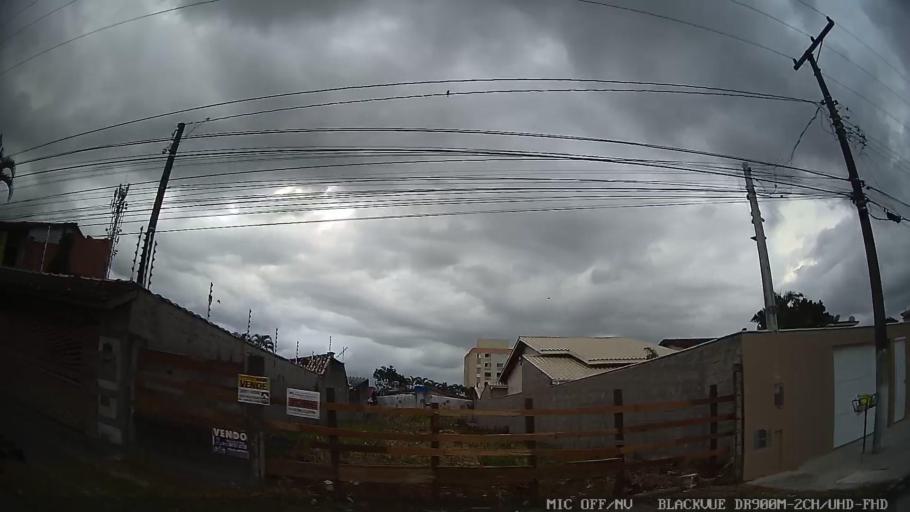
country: BR
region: Sao Paulo
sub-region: Caraguatatuba
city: Caraguatatuba
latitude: -23.6875
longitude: -45.4318
